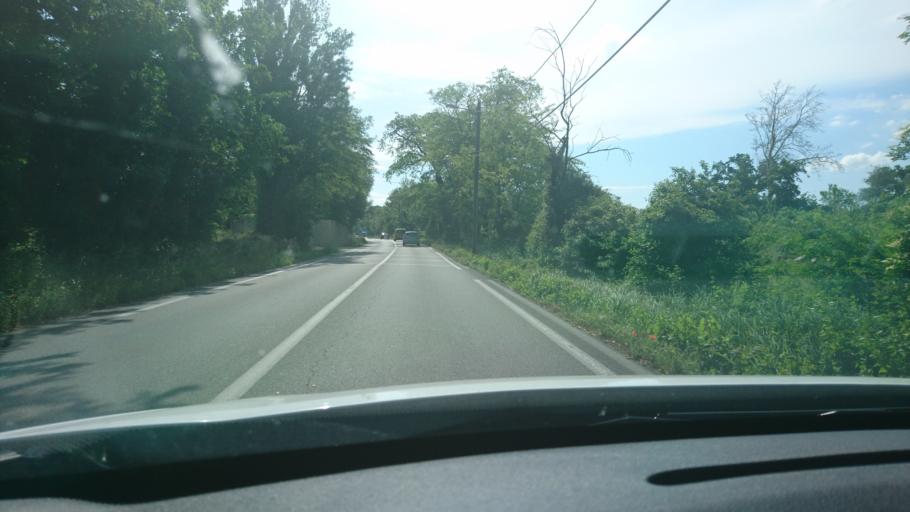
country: FR
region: Provence-Alpes-Cote d'Azur
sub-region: Departement du Vaucluse
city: Le Pontet
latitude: 43.9496
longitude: 4.8670
